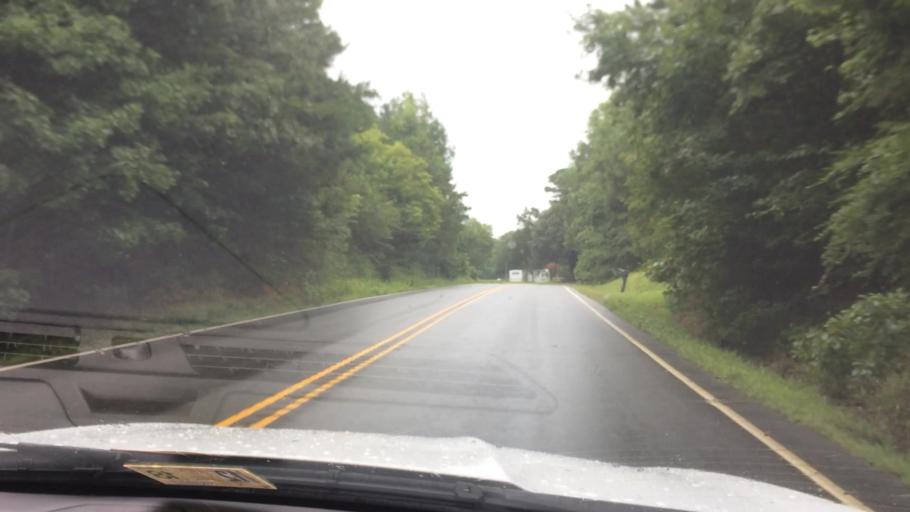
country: US
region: Virginia
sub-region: King William County
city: West Point
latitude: 37.5566
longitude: -76.7404
